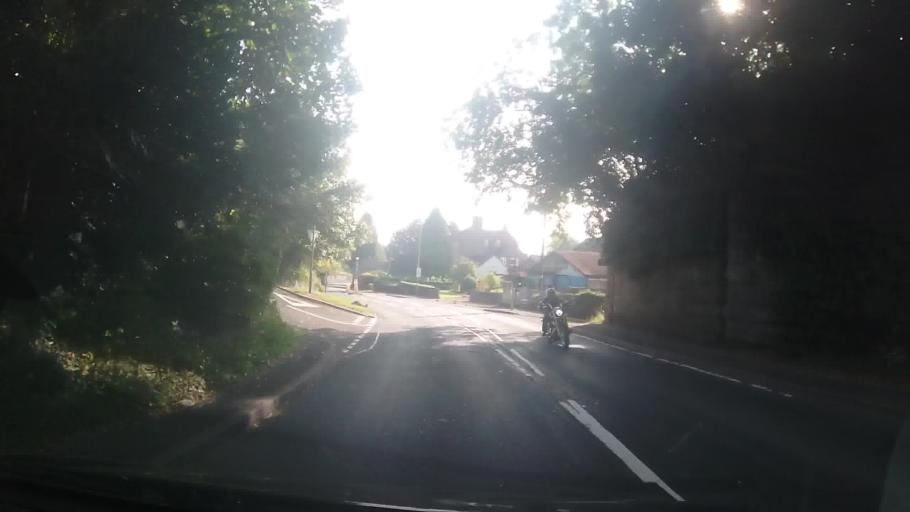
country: GB
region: England
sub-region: Shropshire
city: Much Wenlock
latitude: 52.5946
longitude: -2.5670
